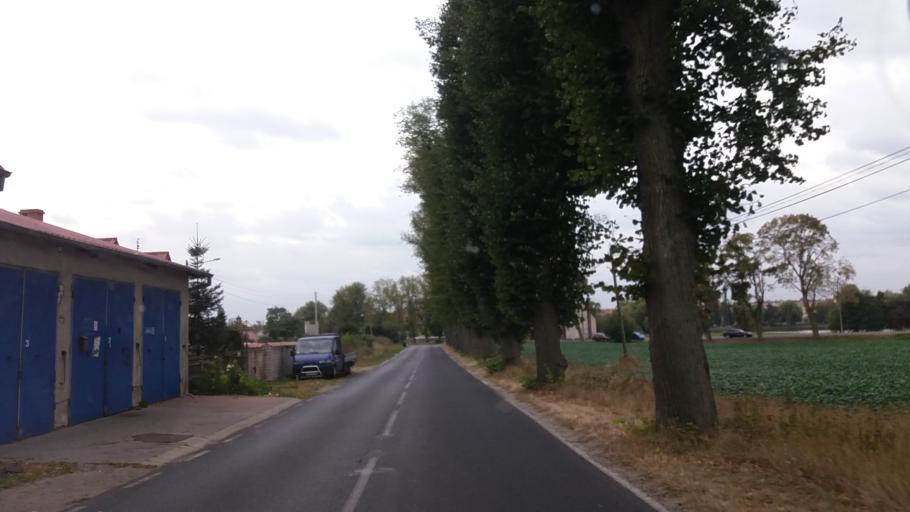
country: PL
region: Lubusz
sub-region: Powiat strzelecko-drezdenecki
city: Strzelce Krajenskie
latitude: 52.8848
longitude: 15.5410
